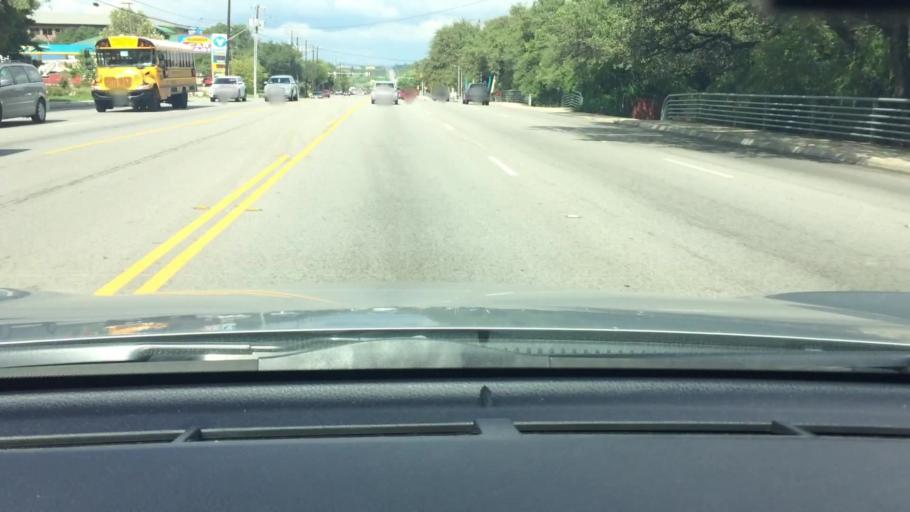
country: US
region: Texas
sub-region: Bexar County
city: Shavano Park
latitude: 29.5477
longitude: -98.5756
